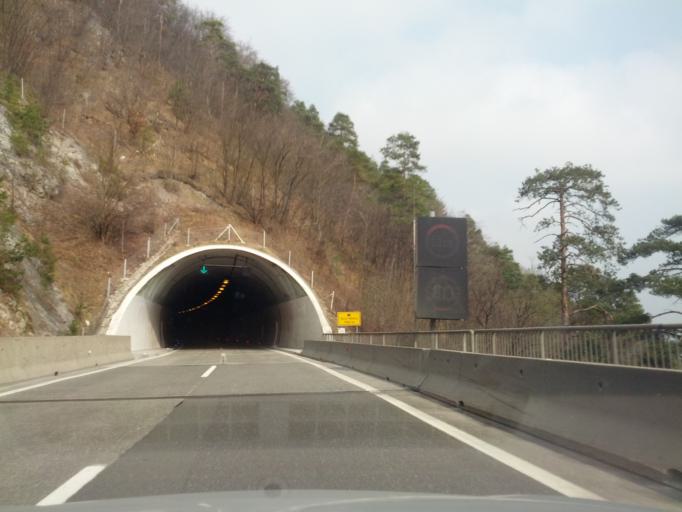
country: SI
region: Slovenska Konjice
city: Slovenske Konjice
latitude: 46.3103
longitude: 15.4559
